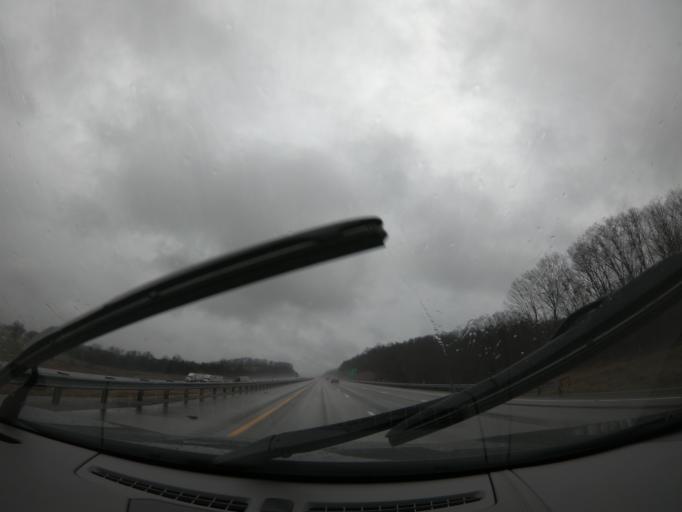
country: US
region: Kentucky
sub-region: Barren County
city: Cave City
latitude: 37.1111
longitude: -86.0328
